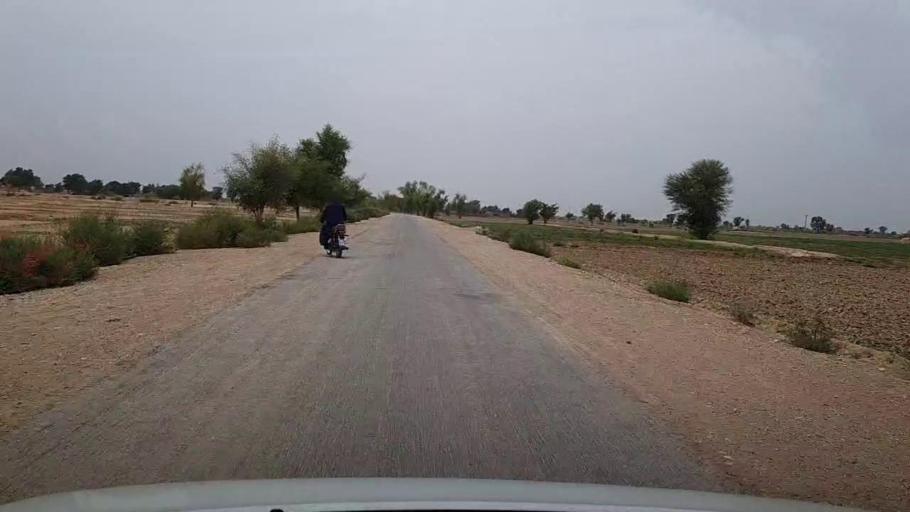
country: PK
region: Sindh
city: Sehwan
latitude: 26.3155
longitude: 67.7559
